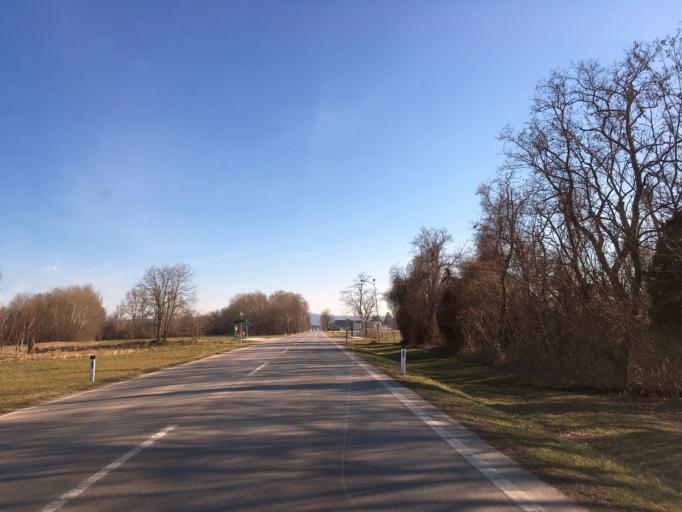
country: AT
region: Lower Austria
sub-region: Politischer Bezirk Baden
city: Ebreichsdorf
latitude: 47.9428
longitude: 16.4127
